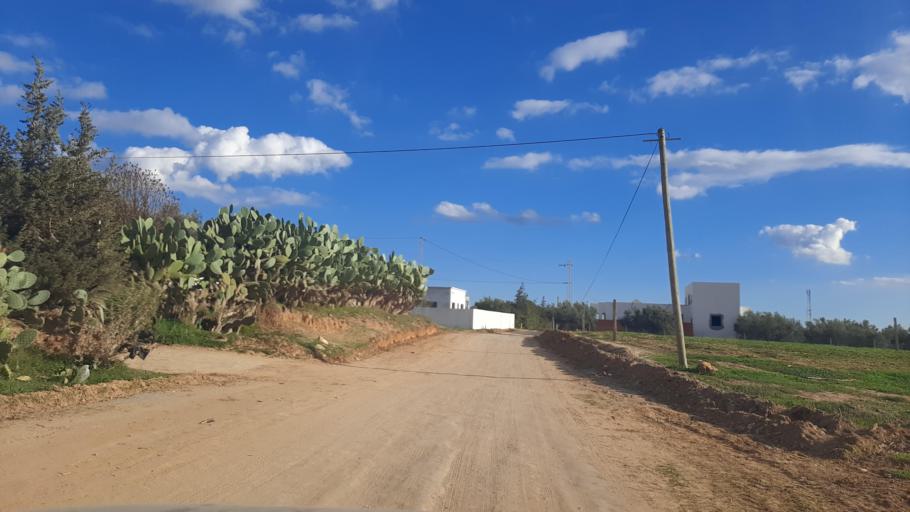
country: TN
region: Nabul
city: Al Hammamat
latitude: 36.4216
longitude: 10.5097
